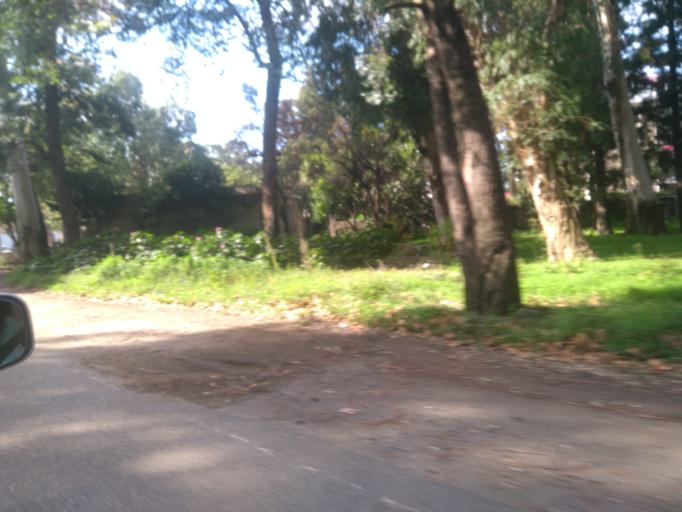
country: GE
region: Ajaria
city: Khelvachauri
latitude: 41.5765
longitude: 41.6615
